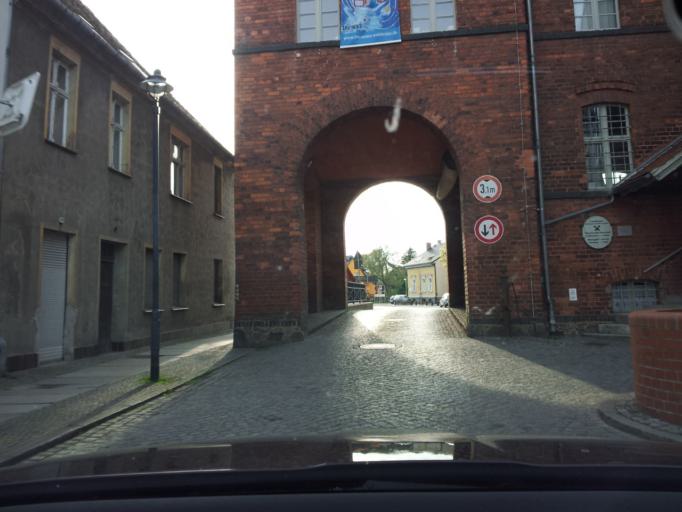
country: DE
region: Brandenburg
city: Lubbenau
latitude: 51.8694
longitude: 13.9659
